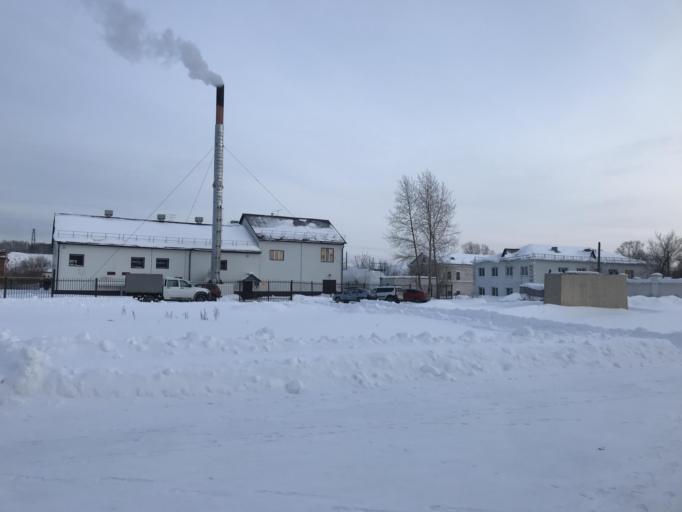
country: RU
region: Tjumen
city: Tobol'sk
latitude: 58.1941
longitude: 68.2439
